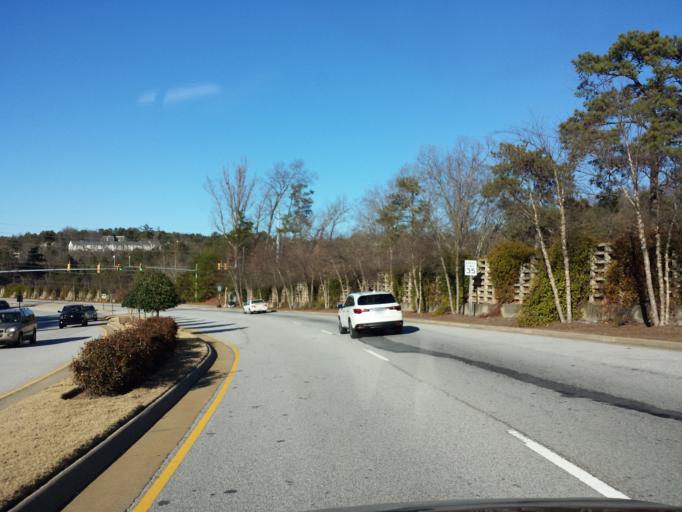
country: US
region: Georgia
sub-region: Cobb County
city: Vinings
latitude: 33.8827
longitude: -84.4522
